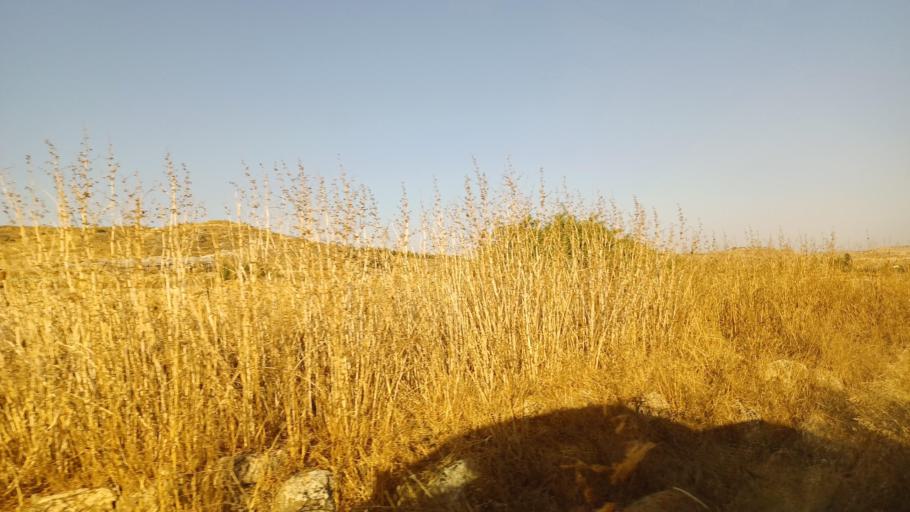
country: CY
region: Larnaka
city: Athienou
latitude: 35.0505
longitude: 33.5087
